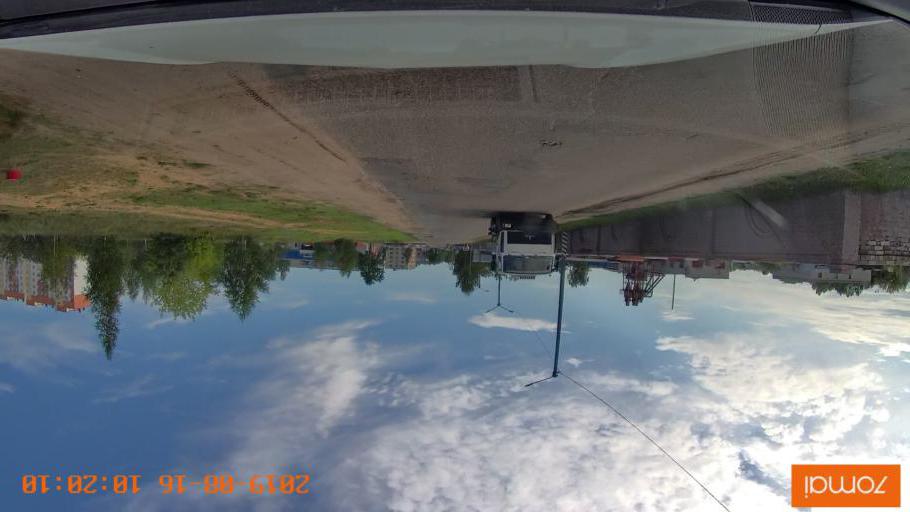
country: BY
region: Mogilev
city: Asipovichy
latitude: 53.3027
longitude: 28.6630
